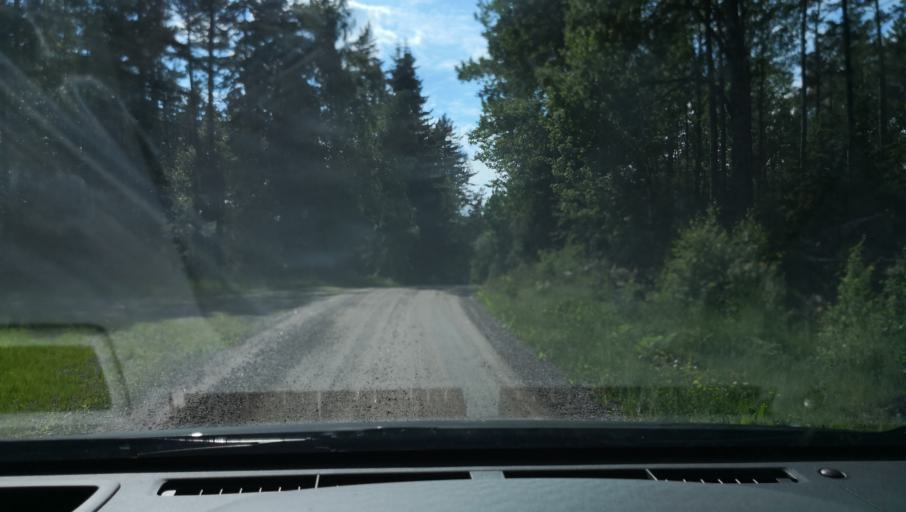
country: SE
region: Uppsala
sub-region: Enkopings Kommun
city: Orsundsbro
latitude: 59.8363
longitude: 17.2580
